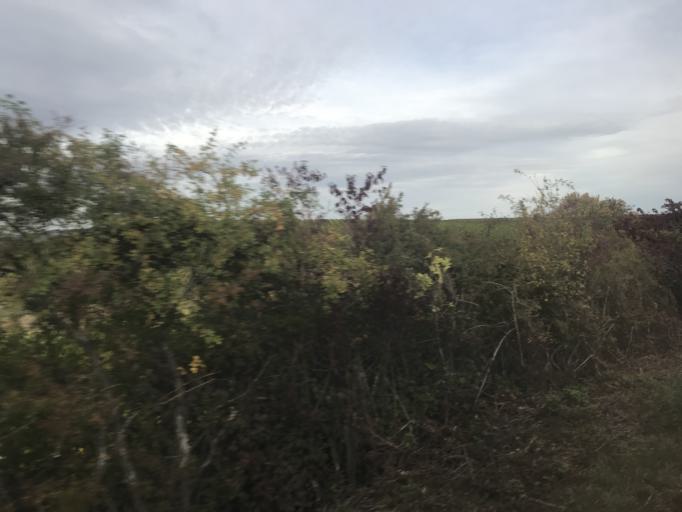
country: DE
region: Rheinland-Pfalz
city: Armsheim
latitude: 49.8229
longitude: 8.0721
